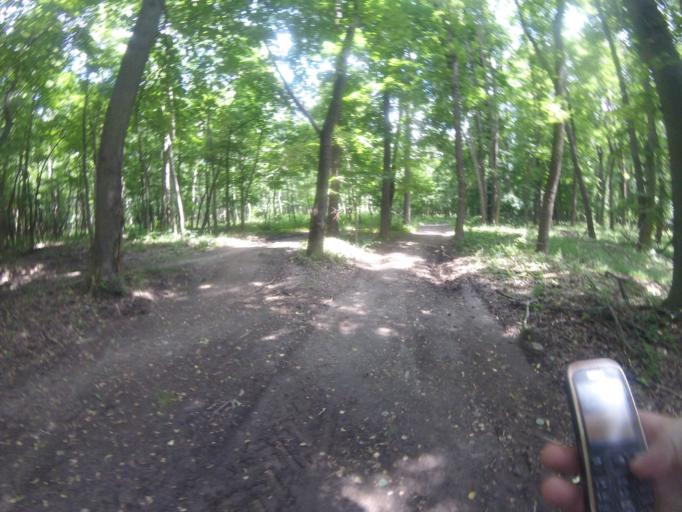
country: HU
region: Fejer
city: Szarliget
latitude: 47.4967
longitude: 18.4447
